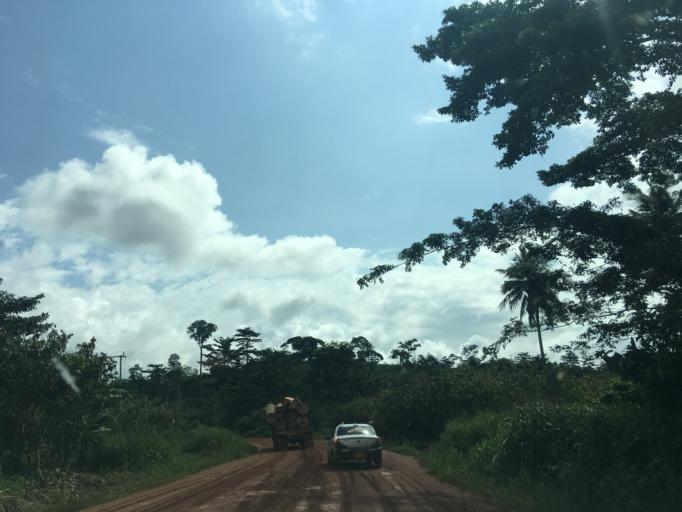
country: GH
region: Western
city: Wassa-Akropong
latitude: 5.7888
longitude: -2.3875
